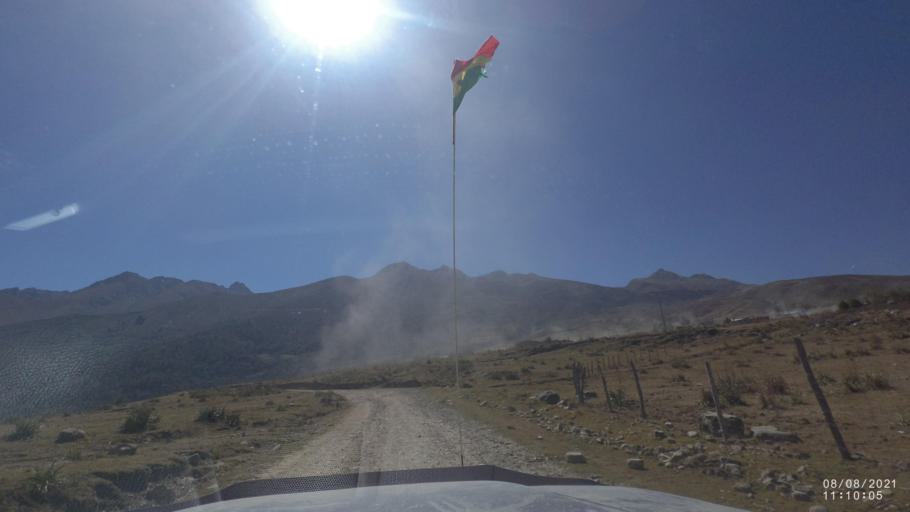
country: BO
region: Cochabamba
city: Colchani
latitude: -16.7603
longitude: -66.6718
